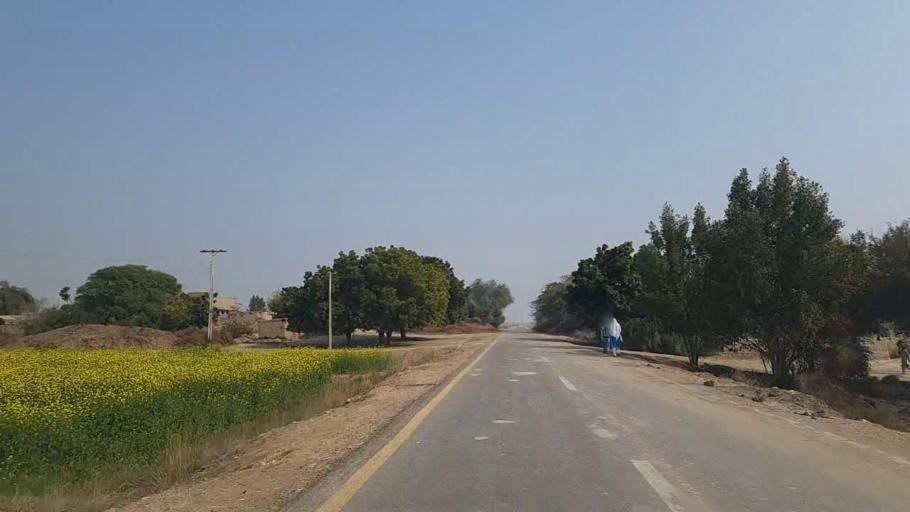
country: PK
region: Sindh
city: Jam Sahib
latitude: 26.3725
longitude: 68.5181
